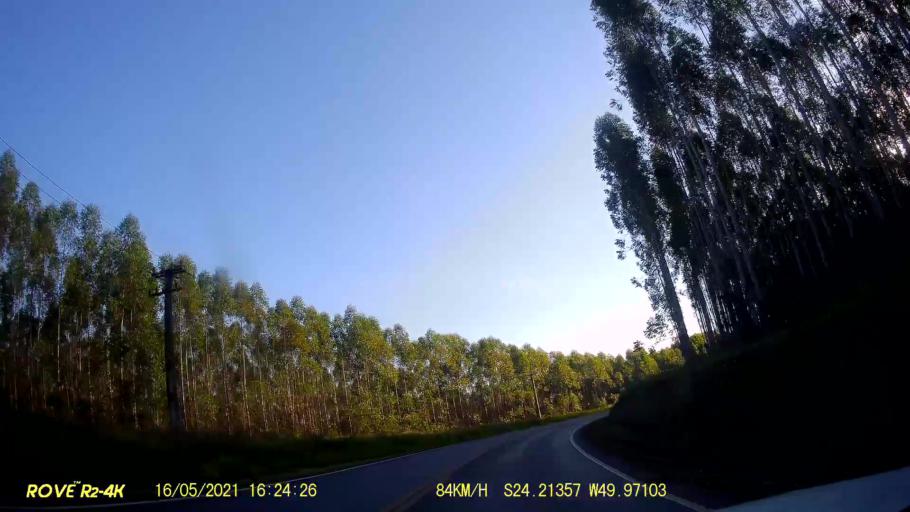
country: BR
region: Parana
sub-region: Jaguariaiva
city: Jaguariaiva
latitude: -24.2135
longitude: -49.9716
